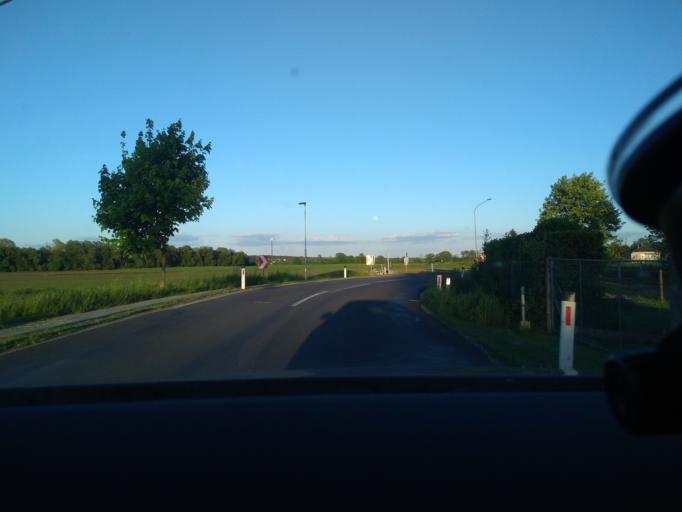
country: AT
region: Styria
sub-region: Politischer Bezirk Voitsberg
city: Mooskirchen
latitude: 46.9901
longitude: 15.2817
